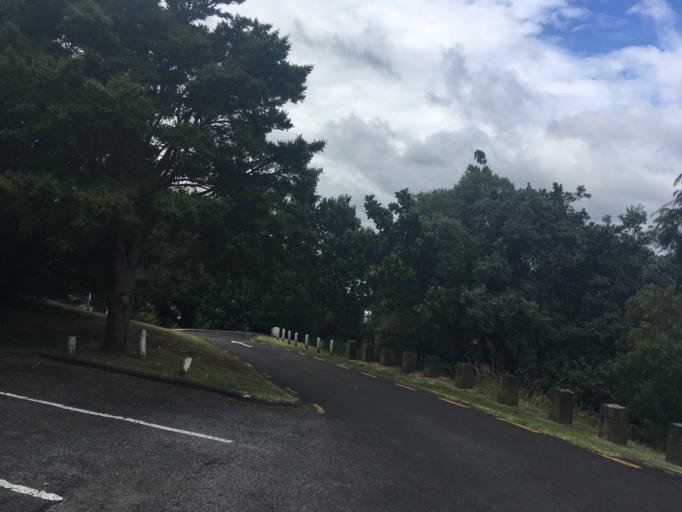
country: NZ
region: Auckland
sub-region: Auckland
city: Auckland
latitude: -36.8279
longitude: 174.7985
